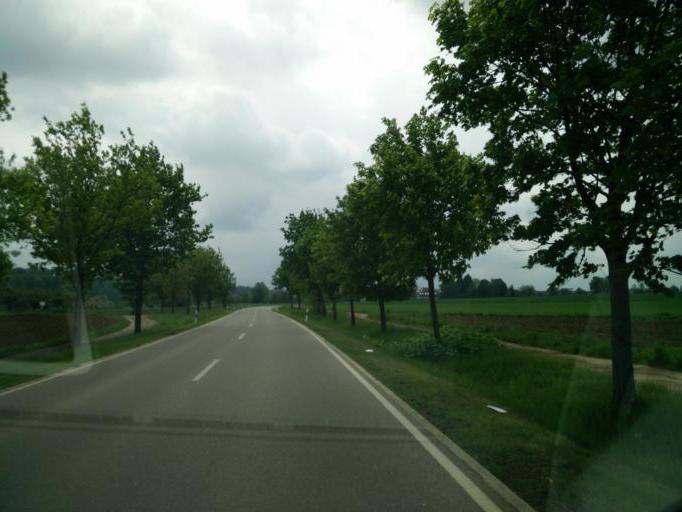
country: DE
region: Baden-Wuerttemberg
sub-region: Tuebingen Region
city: Kusterdingen
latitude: 48.4919
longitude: 9.1192
